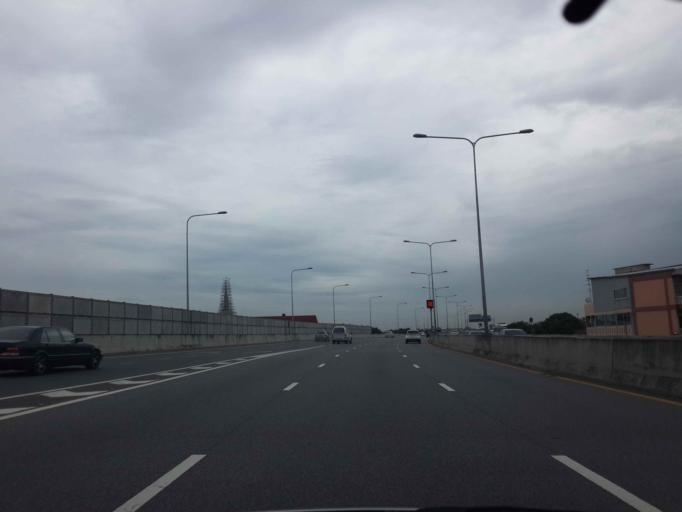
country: TH
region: Bangkok
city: Bang Khen
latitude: 13.8582
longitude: 100.6425
